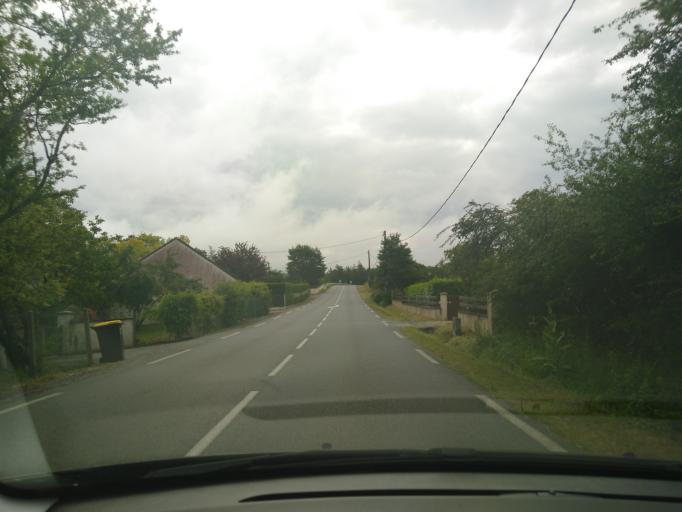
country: FR
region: Limousin
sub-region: Departement de la Correze
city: Cosnac
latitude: 45.1027
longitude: 1.5625
